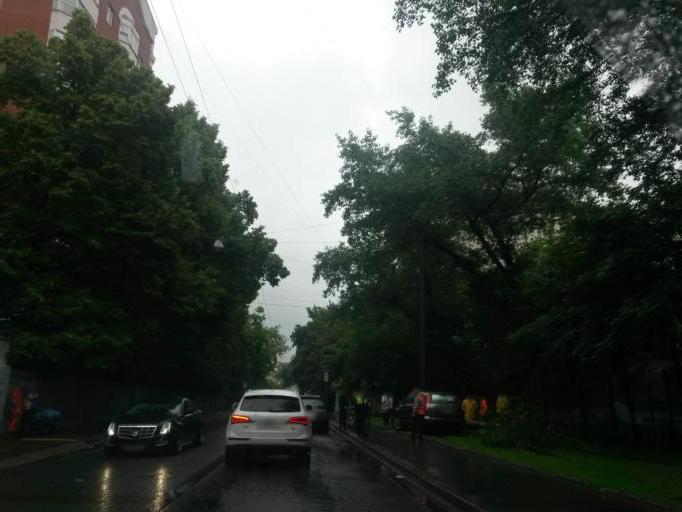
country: RU
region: Moscow
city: Moscow
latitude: 55.7337
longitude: 37.6133
